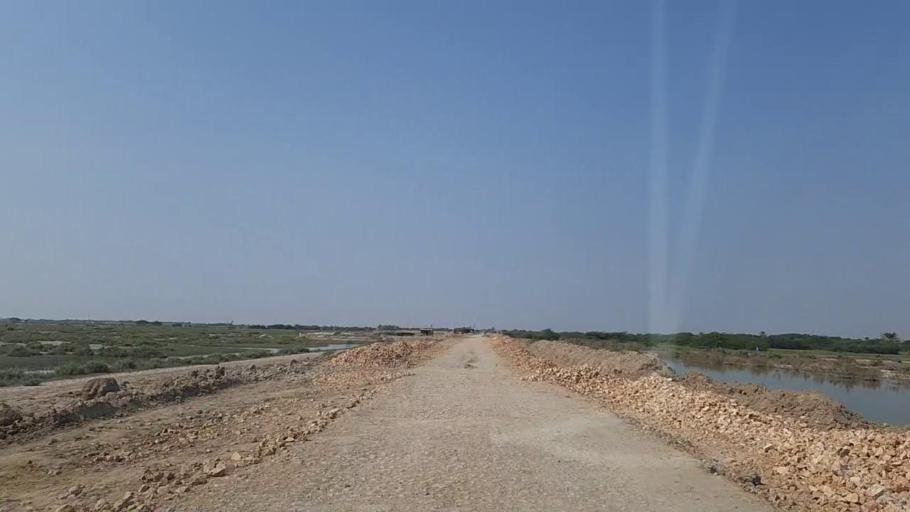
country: PK
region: Sindh
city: Chuhar Jamali
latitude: 24.1940
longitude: 67.8394
